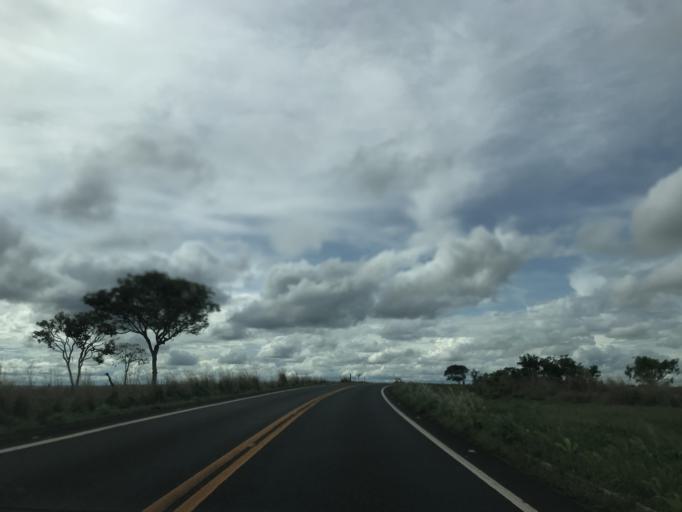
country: BR
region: Goias
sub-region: Piracanjuba
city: Piracanjuba
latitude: -17.4313
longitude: -48.8021
